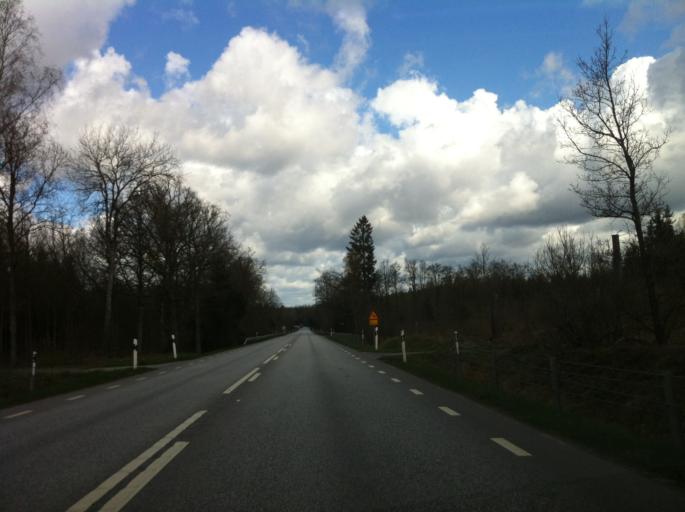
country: SE
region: Skane
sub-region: Horby Kommun
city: Hoerby
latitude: 55.8914
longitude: 13.6250
